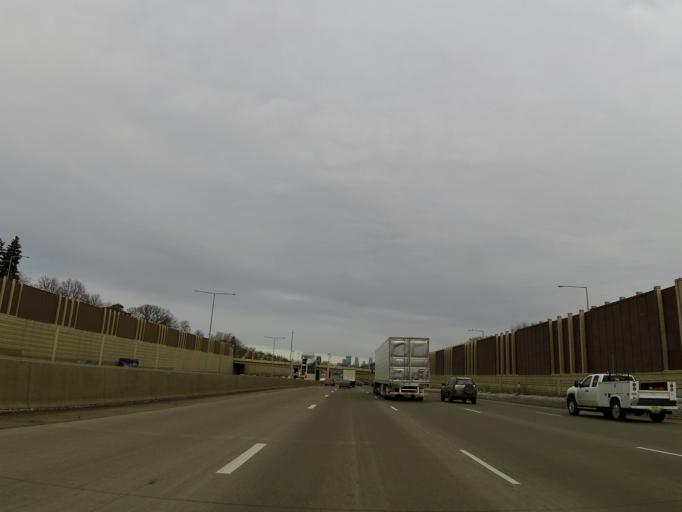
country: US
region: Minnesota
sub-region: Hennepin County
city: Richfield
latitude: 44.9173
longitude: -93.2745
